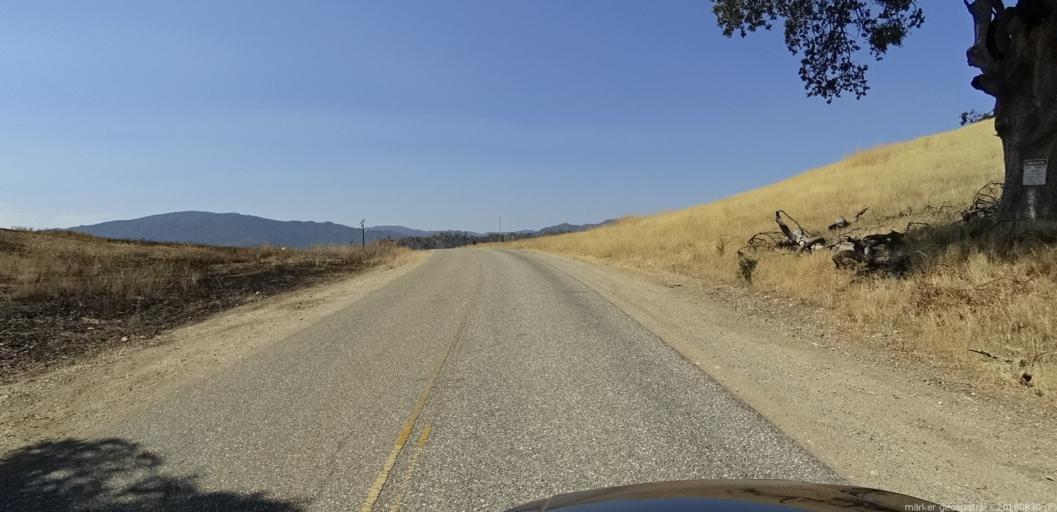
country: US
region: California
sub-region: Monterey County
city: King City
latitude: 35.9773
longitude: -121.2634
